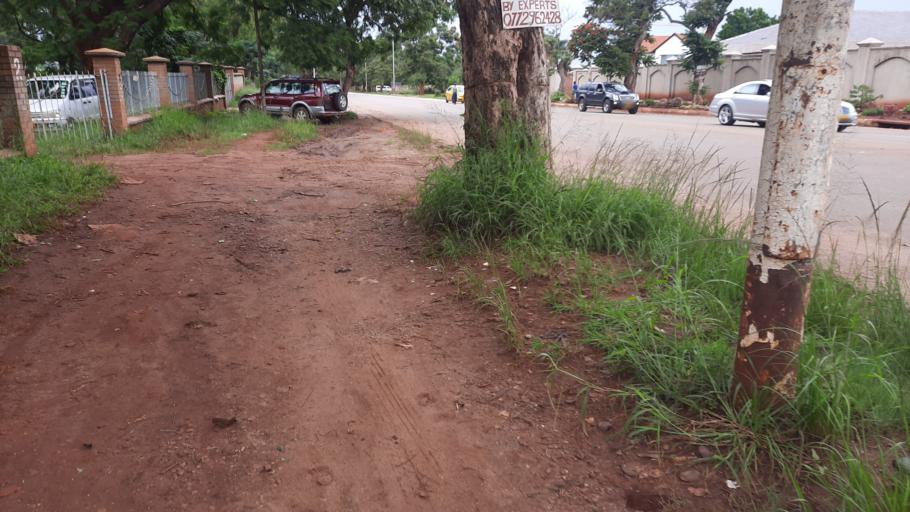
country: ZW
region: Harare
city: Harare
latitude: -17.8195
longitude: 31.0308
